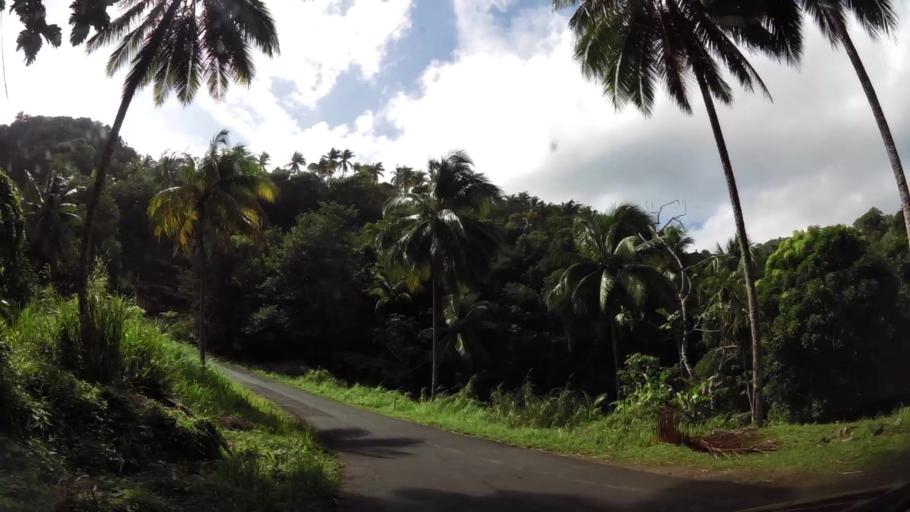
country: DM
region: Saint David
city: Castle Bruce
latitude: 15.4738
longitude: -61.2517
